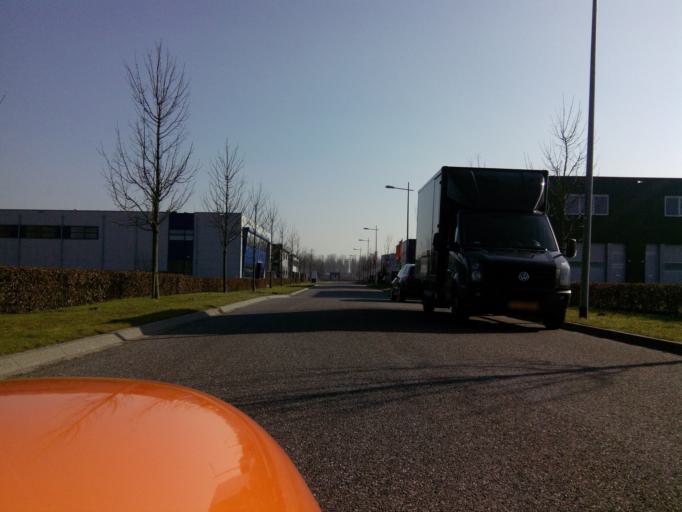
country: NL
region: Flevoland
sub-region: Gemeente Zeewolde
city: Zeewolde
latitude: 52.3514
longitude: 5.4932
